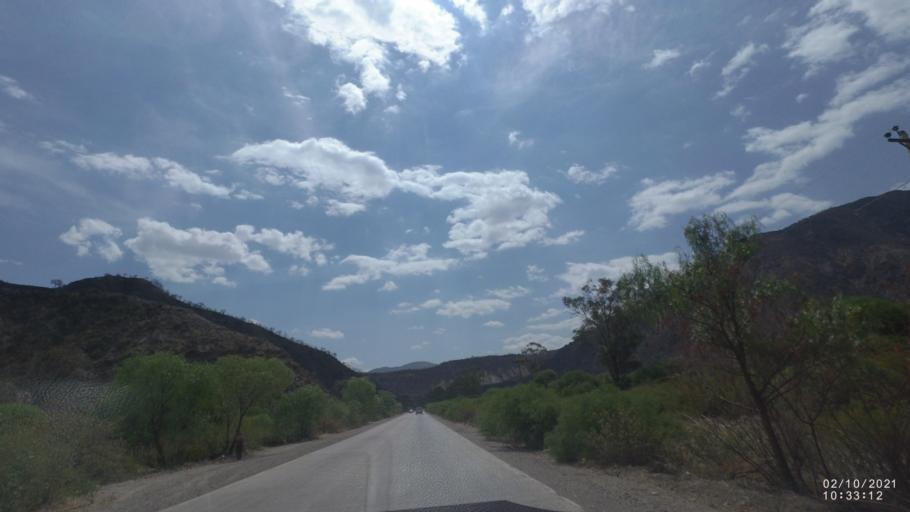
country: BO
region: Cochabamba
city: Capinota
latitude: -17.6824
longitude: -66.2564
